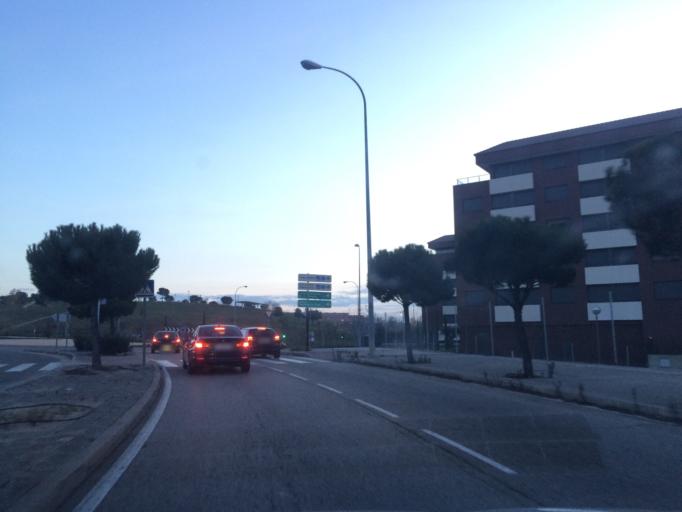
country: ES
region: Madrid
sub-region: Provincia de Madrid
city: Fuencarral-El Pardo
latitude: 40.4966
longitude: -3.7199
